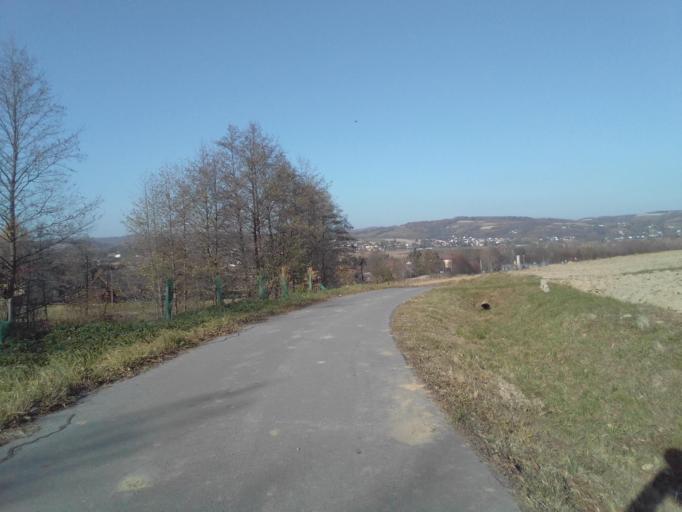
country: PL
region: Subcarpathian Voivodeship
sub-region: Powiat strzyzowski
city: Wisniowa
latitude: 49.8541
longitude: 21.6609
